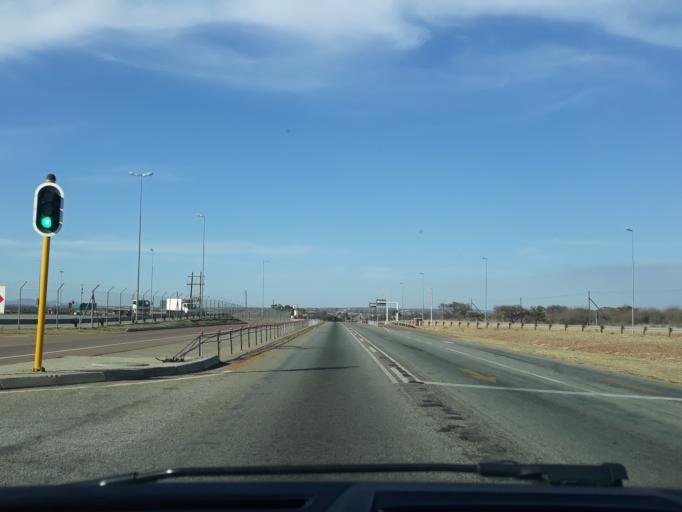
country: ZA
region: Limpopo
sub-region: Capricorn District Municipality
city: Polokwane
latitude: -23.9545
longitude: 29.3955
